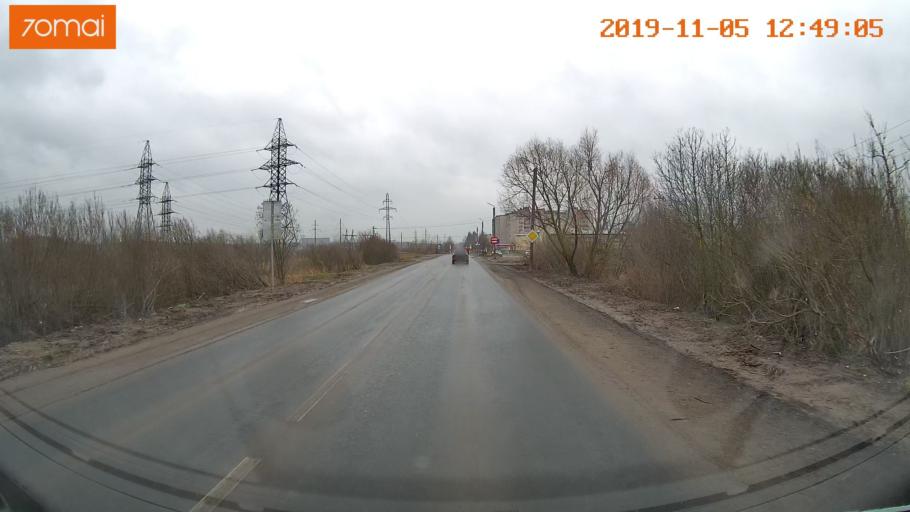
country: RU
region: Ivanovo
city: Kokhma
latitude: 56.9570
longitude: 41.1021
